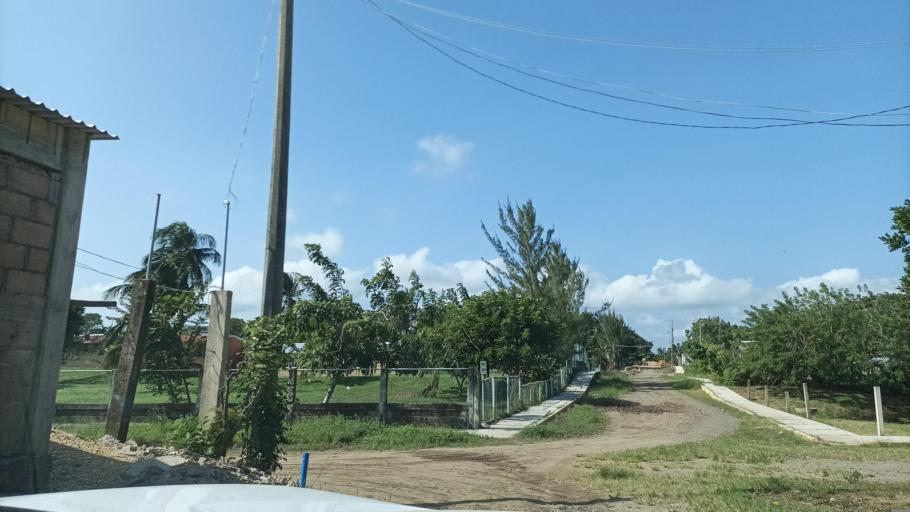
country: MX
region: Veracruz
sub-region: Coatzacoalcos
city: Fraccionamiento Ciudad Olmeca
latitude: 18.2169
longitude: -94.6133
